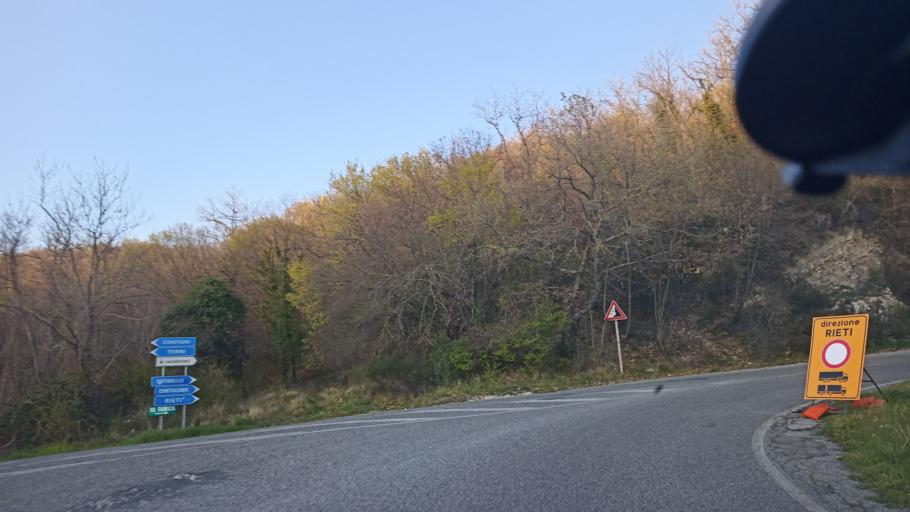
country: IT
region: Latium
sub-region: Provincia di Rieti
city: Cottanello
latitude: 42.4133
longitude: 12.6786
